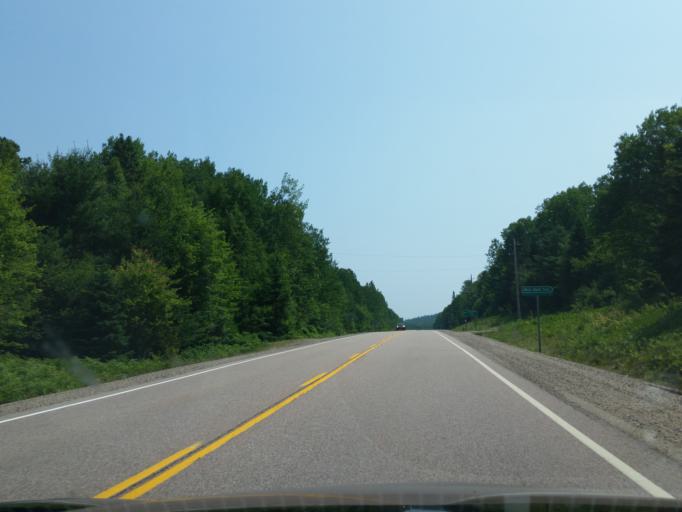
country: CA
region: Ontario
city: Deep River
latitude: 46.1741
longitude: -77.7844
